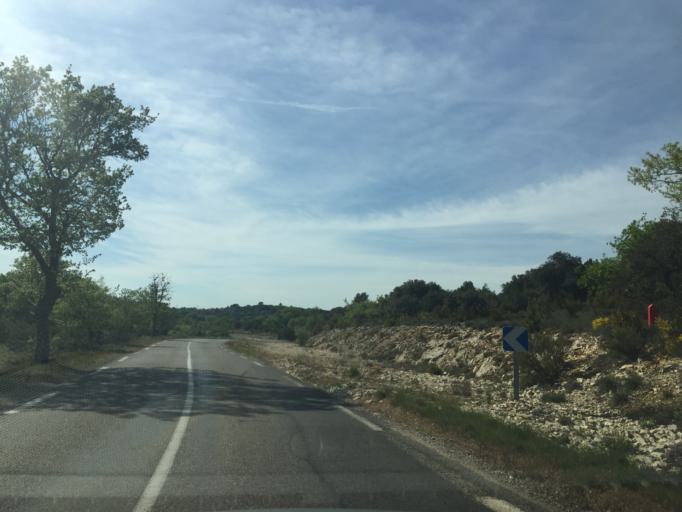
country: FR
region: Provence-Alpes-Cote d'Azur
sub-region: Departement du Var
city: Ginasservis
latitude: 43.6706
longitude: 5.8690
